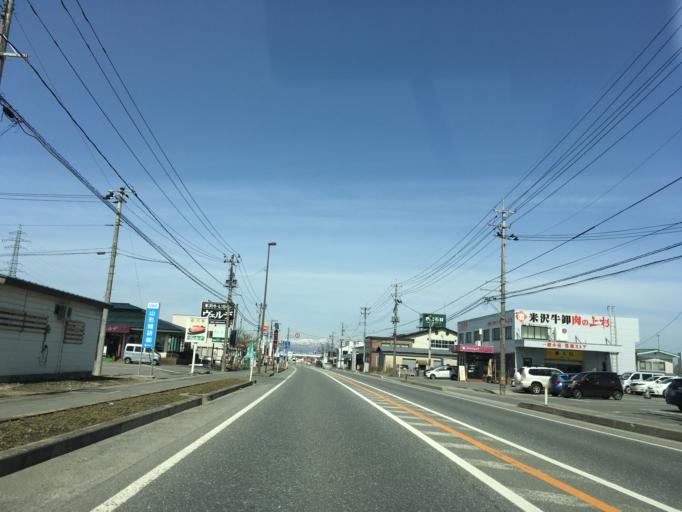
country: JP
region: Yamagata
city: Yonezawa
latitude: 37.9182
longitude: 140.1315
